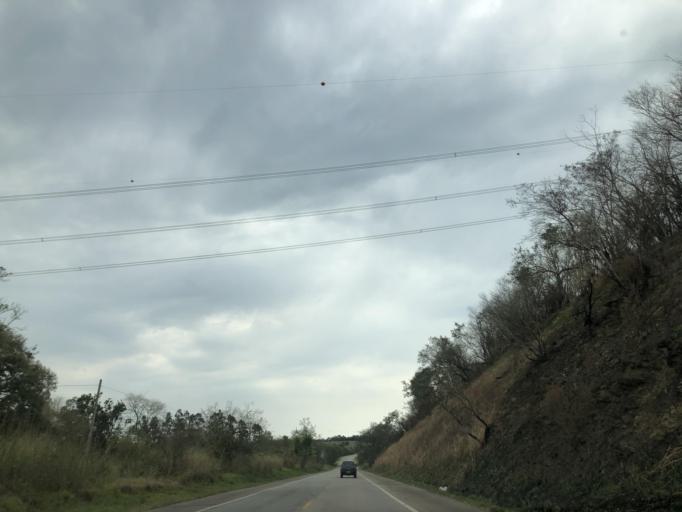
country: BR
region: Sao Paulo
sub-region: Salto De Pirapora
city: Salto de Pirapora
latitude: -23.7189
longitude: -47.6383
